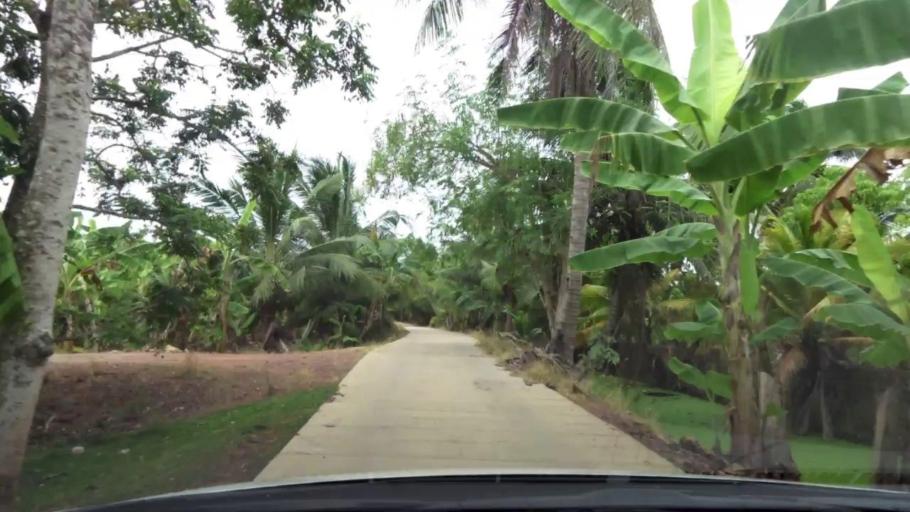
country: TH
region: Ratchaburi
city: Damnoen Saduak
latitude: 13.5558
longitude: 99.9971
